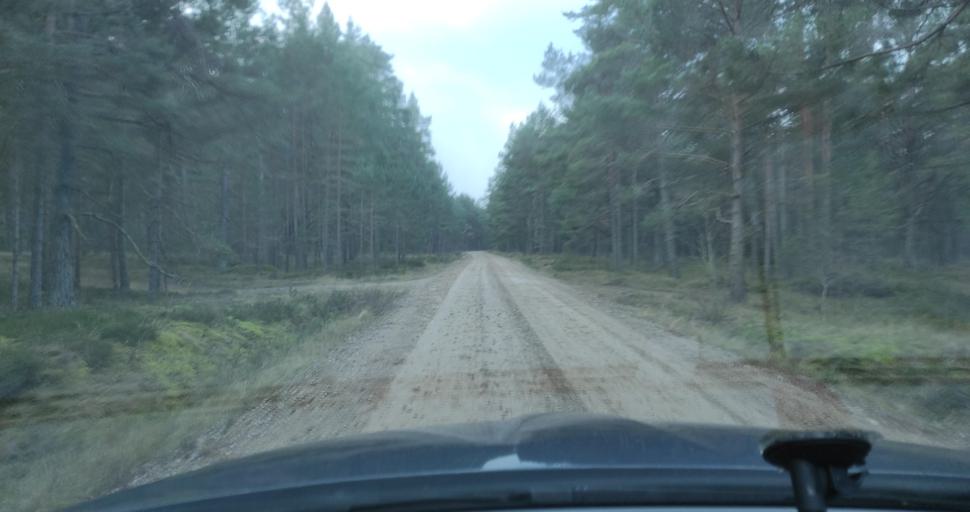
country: LV
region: Pavilostas
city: Pavilosta
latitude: 56.8297
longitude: 21.0714
